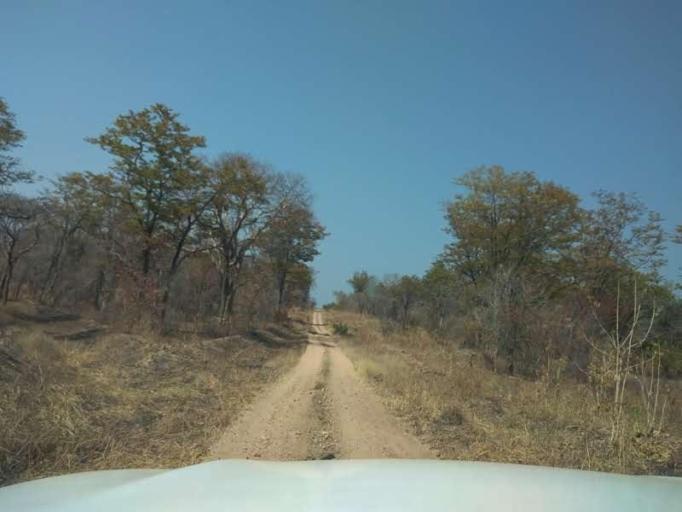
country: ZM
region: Eastern
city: Nyimba
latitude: -14.1423
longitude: 30.1383
